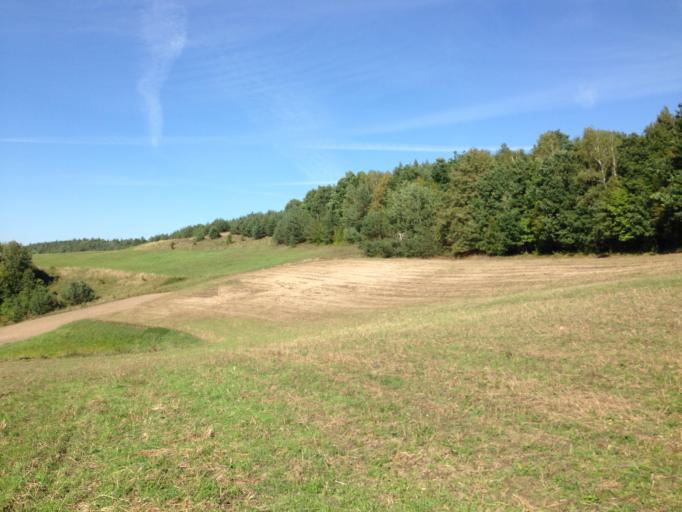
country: PL
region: Warmian-Masurian Voivodeship
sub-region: Powiat dzialdowski
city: Lidzbark
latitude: 53.2278
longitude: 19.7469
